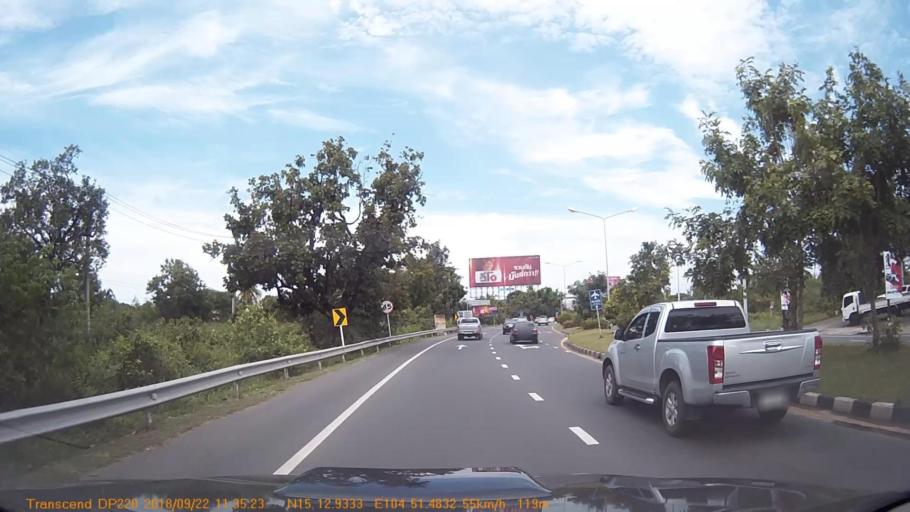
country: TH
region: Changwat Ubon Ratchathani
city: Warin Chamrap
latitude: 15.2156
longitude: 104.8580
